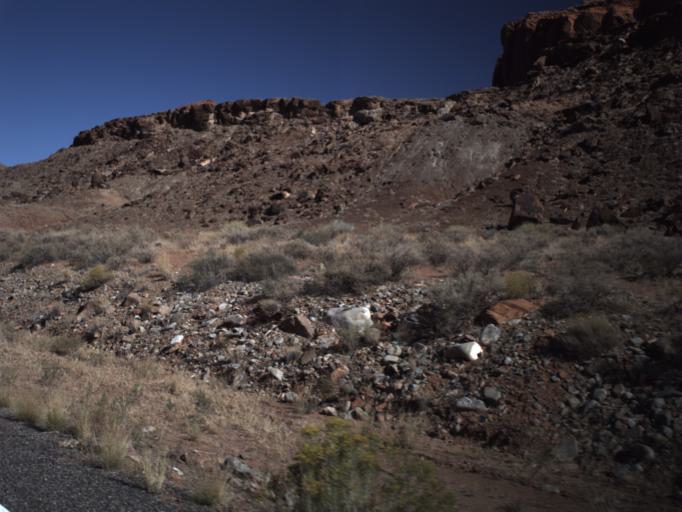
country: US
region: Utah
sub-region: San Juan County
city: Blanding
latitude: 37.9167
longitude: -110.4613
